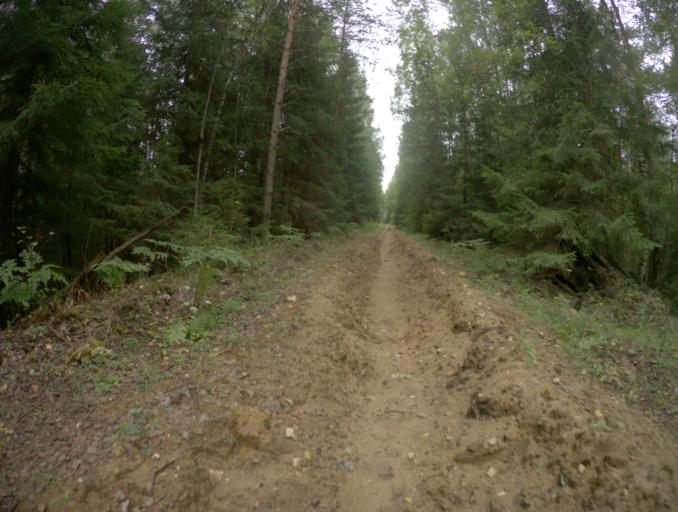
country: RU
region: Vladimir
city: Raduzhnyy
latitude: 55.9785
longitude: 40.2623
